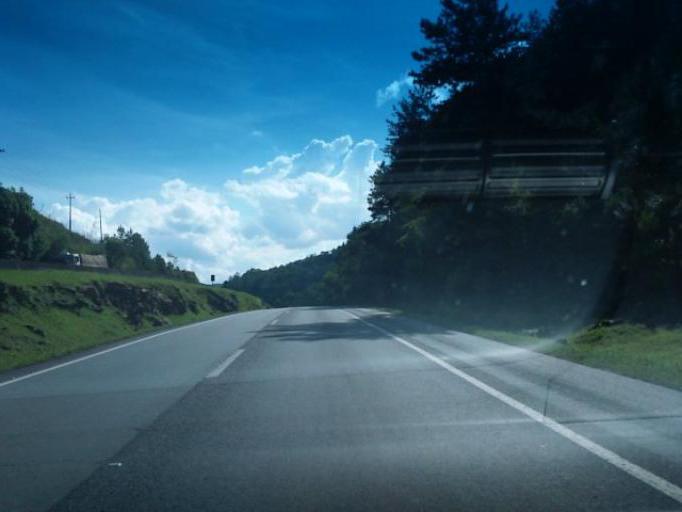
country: BR
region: Parana
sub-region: Campina Grande Do Sul
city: Campina Grande do Sul
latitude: -25.1966
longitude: -48.8922
